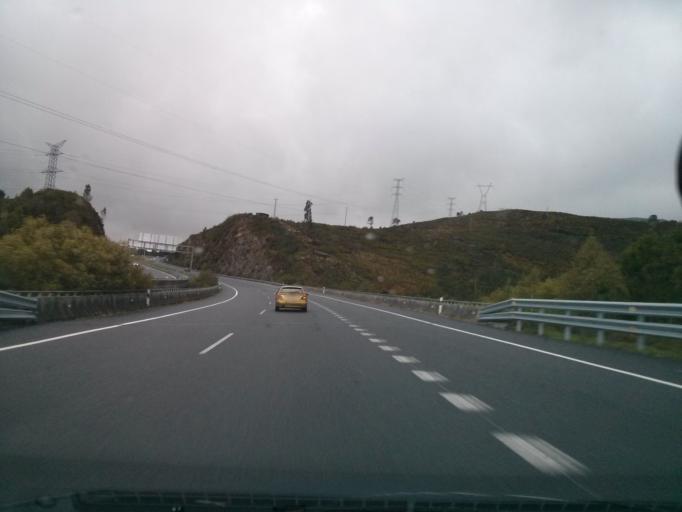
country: ES
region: Galicia
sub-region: Provincia de Ourense
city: Melon
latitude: 42.2684
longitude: -8.2090
